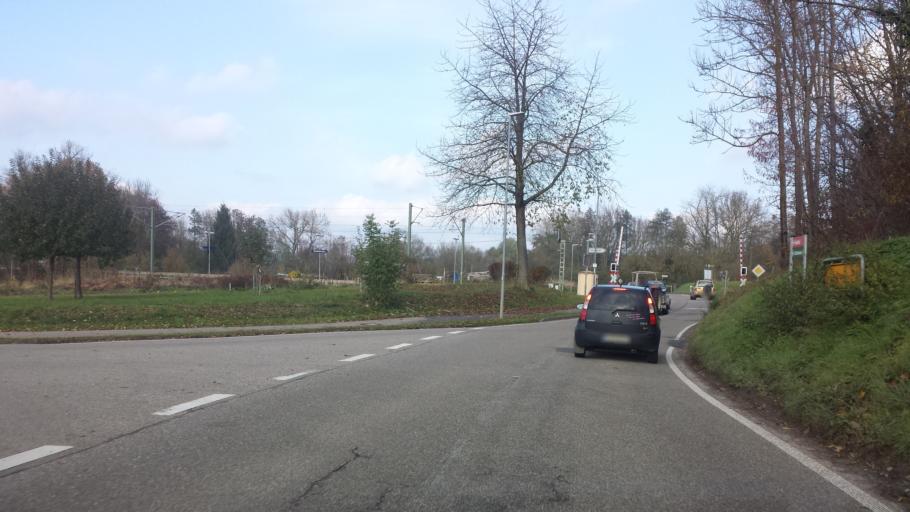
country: DE
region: Baden-Wuerttemberg
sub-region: Karlsruhe Region
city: Zaisenhausen
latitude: 49.1087
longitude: 8.7452
